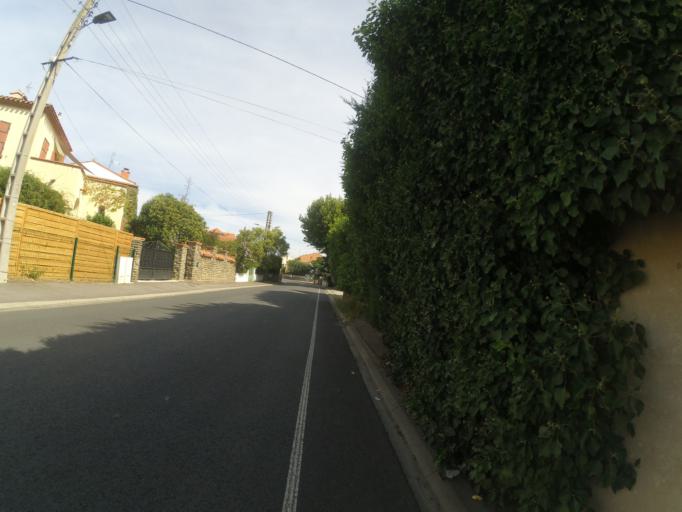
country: FR
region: Languedoc-Roussillon
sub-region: Departement des Pyrenees-Orientales
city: Ille-sur-Tet
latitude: 42.6671
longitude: 2.6200
